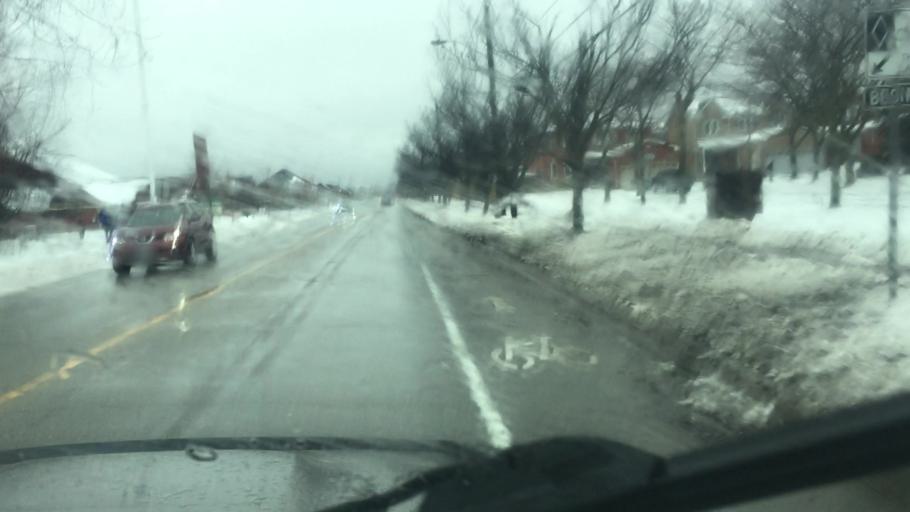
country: CA
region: Ontario
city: Ajax
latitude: 43.8609
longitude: -79.0584
